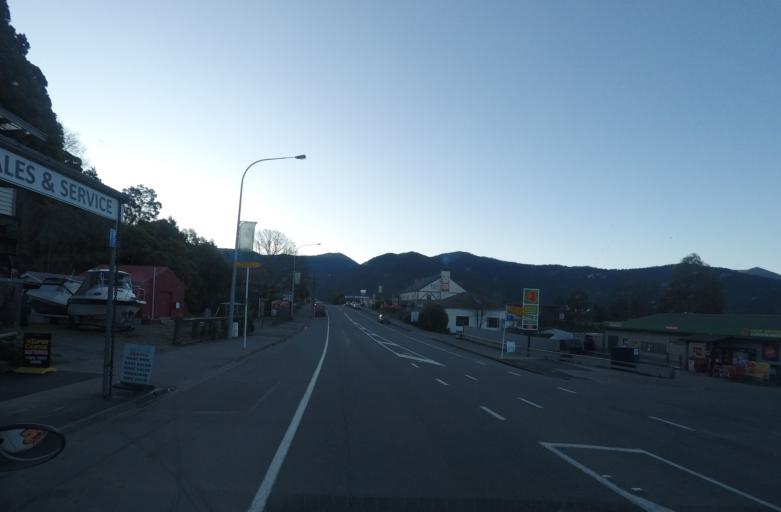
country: NZ
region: Marlborough
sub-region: Marlborough District
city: Picton
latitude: -41.2781
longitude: 173.7666
